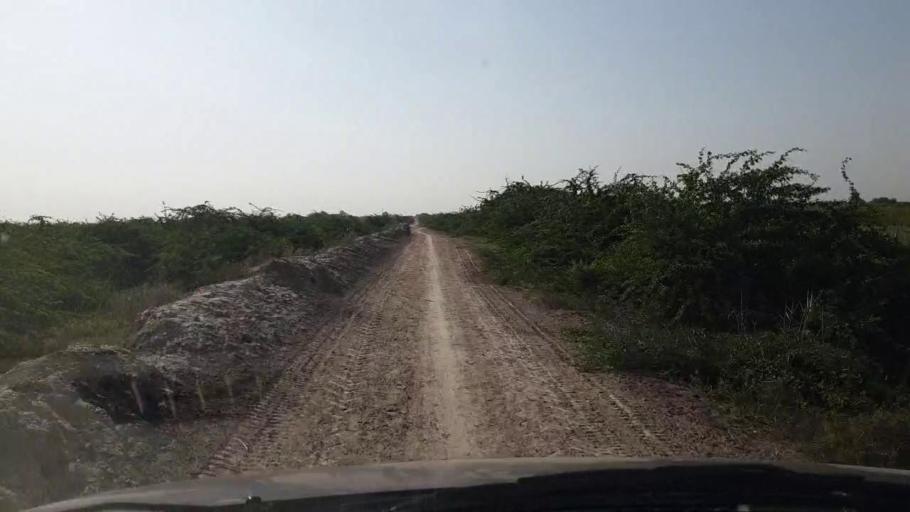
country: PK
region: Sindh
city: Kadhan
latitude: 24.6094
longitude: 69.0732
